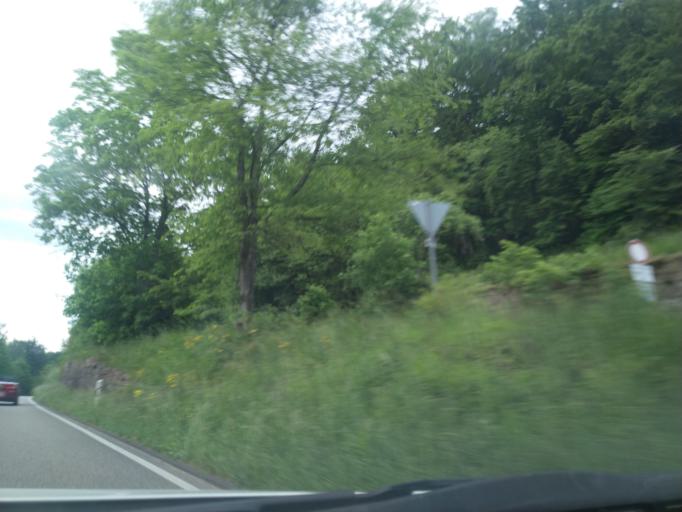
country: DE
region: Baden-Wuerttemberg
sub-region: Karlsruhe Region
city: Hofen an der Enz
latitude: 48.7844
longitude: 8.5795
